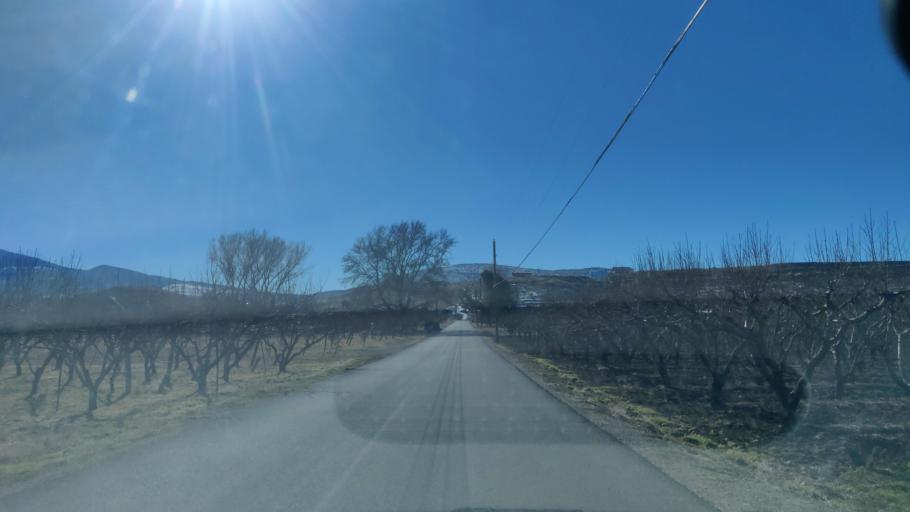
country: US
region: Colorado
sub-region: Mesa County
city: Palisade
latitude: 39.1052
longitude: -108.3343
